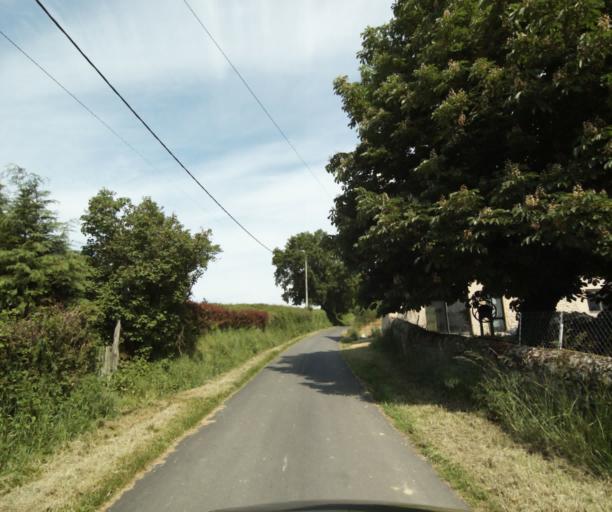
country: FR
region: Bourgogne
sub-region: Departement de Saone-et-Loire
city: Palinges
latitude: 46.5549
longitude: 4.1823
